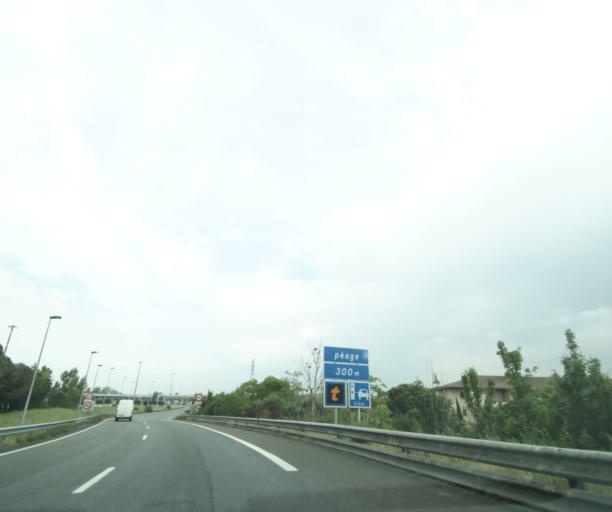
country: FR
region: Midi-Pyrenees
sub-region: Departement de la Haute-Garonne
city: Aucamville
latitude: 43.6554
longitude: 1.4300
